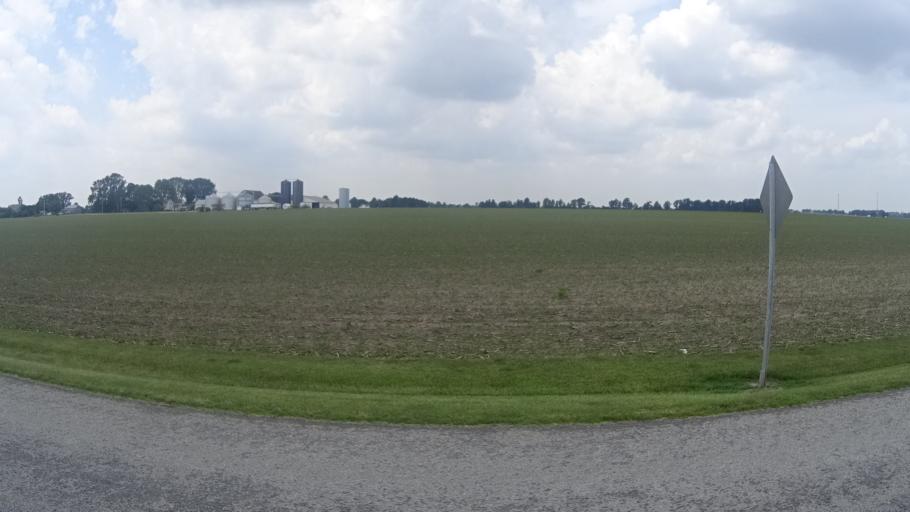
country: US
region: Ohio
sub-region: Erie County
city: Milan
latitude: 41.3251
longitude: -82.6736
